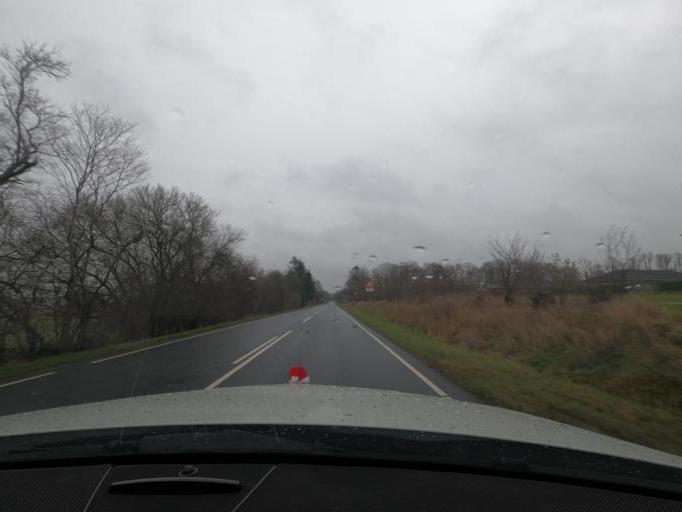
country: DK
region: South Denmark
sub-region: Haderslev Kommune
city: Starup
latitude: 55.2436
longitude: 9.5472
